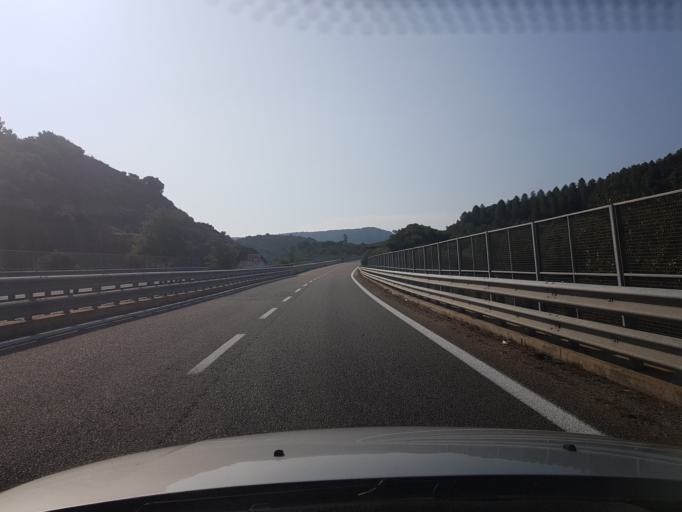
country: IT
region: Sardinia
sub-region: Provincia di Olbia-Tempio
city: Loiri Porto San Paolo
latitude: 40.8277
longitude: 9.5763
